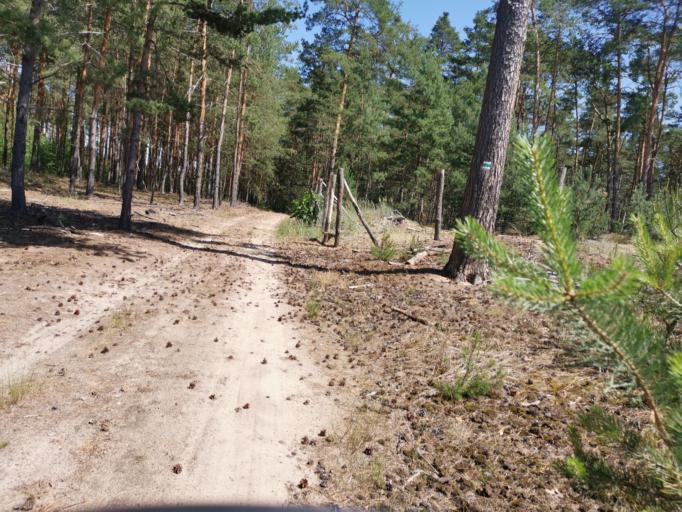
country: CZ
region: South Moravian
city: Bzenec
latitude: 48.9377
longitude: 17.2531
